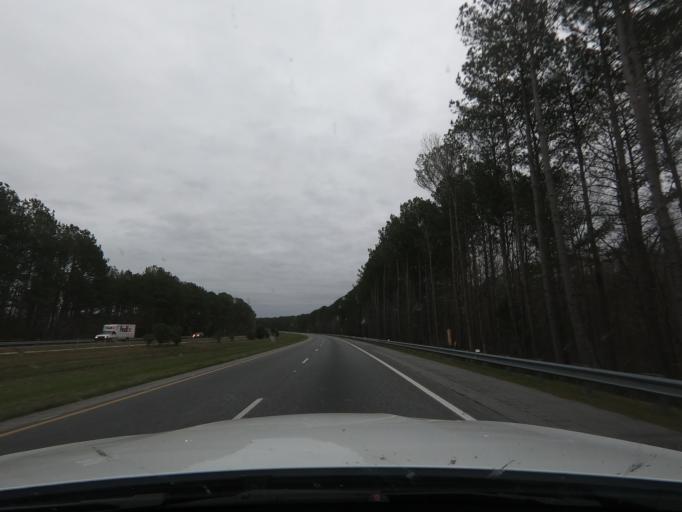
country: US
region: Georgia
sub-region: Harris County
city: Pine Mountain
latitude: 32.8644
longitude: -84.9687
